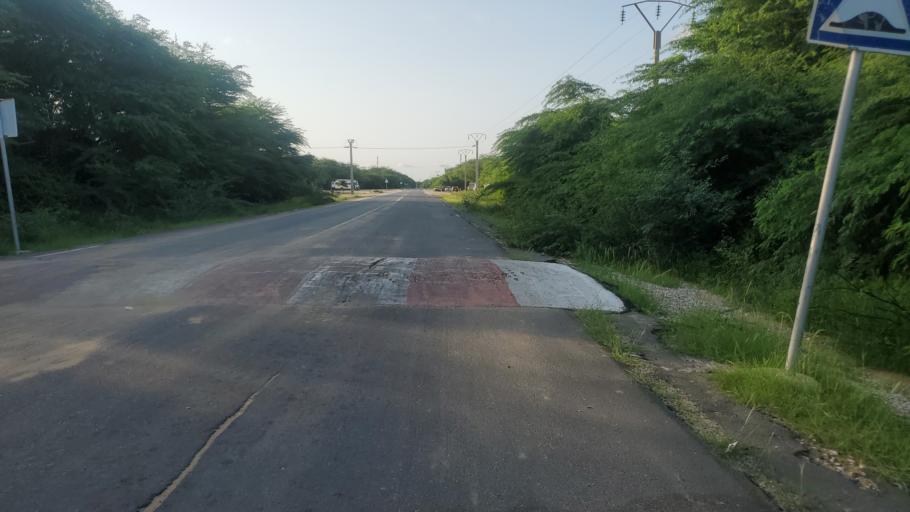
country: SN
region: Saint-Louis
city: Saint-Louis
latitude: 16.1980
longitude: -16.4102
